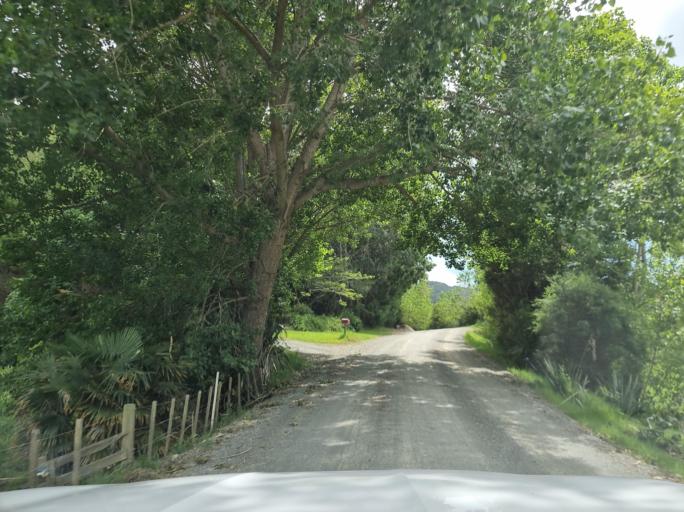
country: NZ
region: Auckland
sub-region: Auckland
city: Wellsford
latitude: -36.0853
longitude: 174.5528
